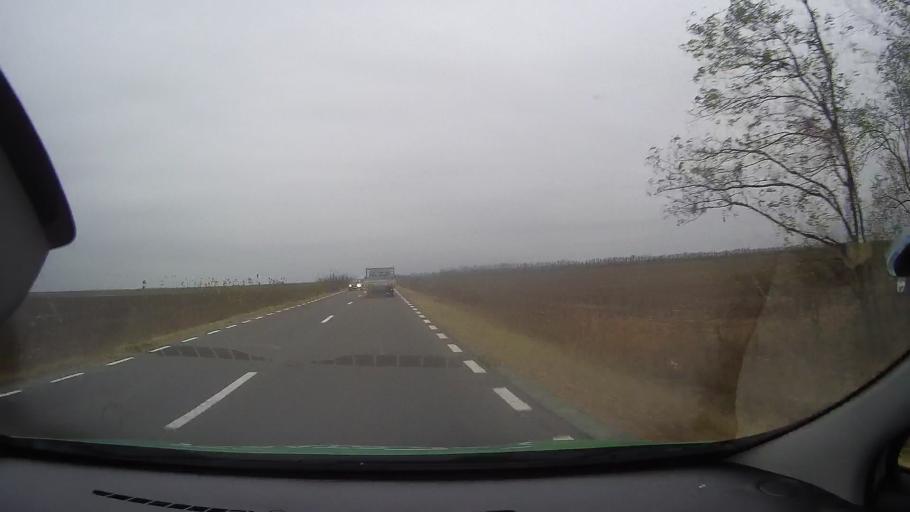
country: RO
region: Ialomita
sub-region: Comuna Scanteia
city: Iazu
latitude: 44.6830
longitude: 27.4186
